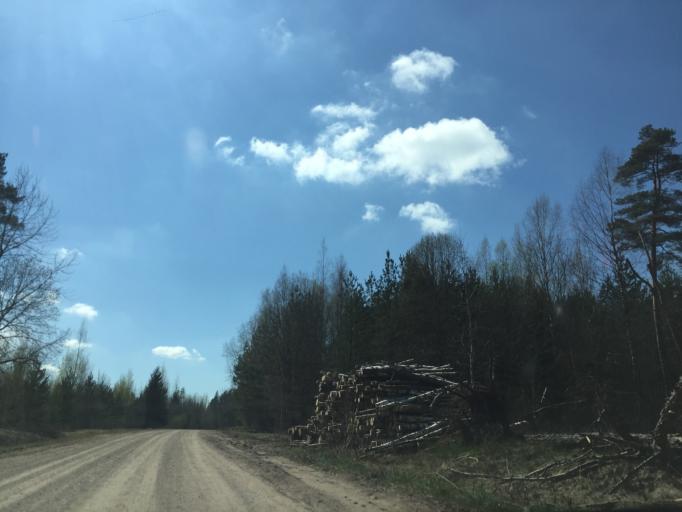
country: LV
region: Smiltene
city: Smiltene
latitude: 57.5733
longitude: 25.9260
